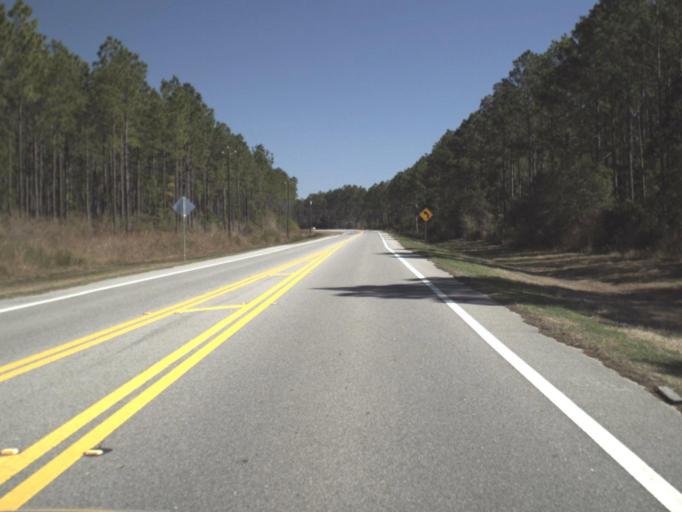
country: US
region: Florida
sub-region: Bay County
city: Laguna Beach
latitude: 30.2986
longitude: -85.8397
